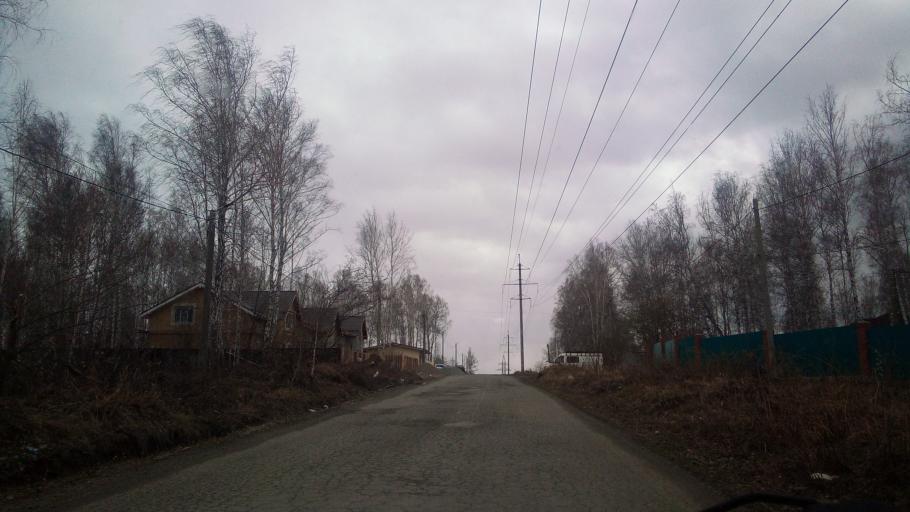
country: RU
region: Chelyabinsk
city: Sargazy
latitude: 55.1319
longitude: 61.2438
